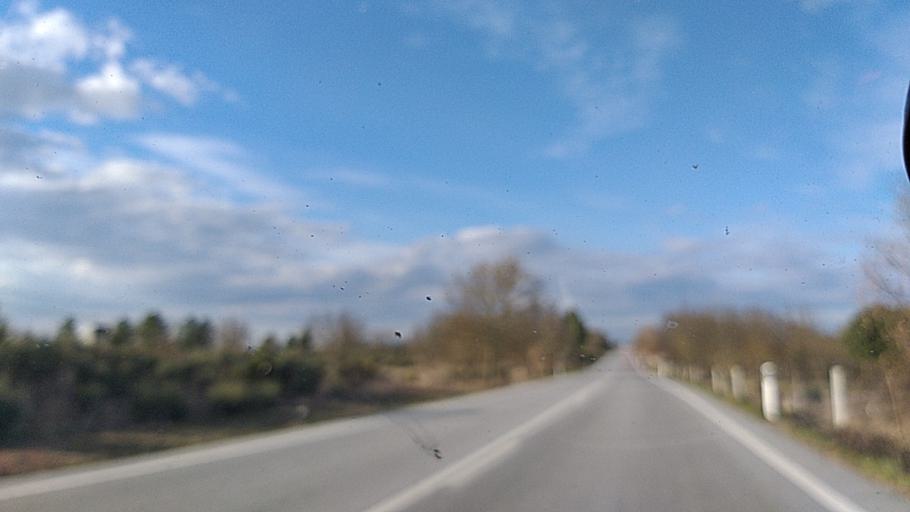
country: ES
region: Castille and Leon
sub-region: Provincia de Salamanca
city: Fuentes de Onoro
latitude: 40.6426
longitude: -6.8561
